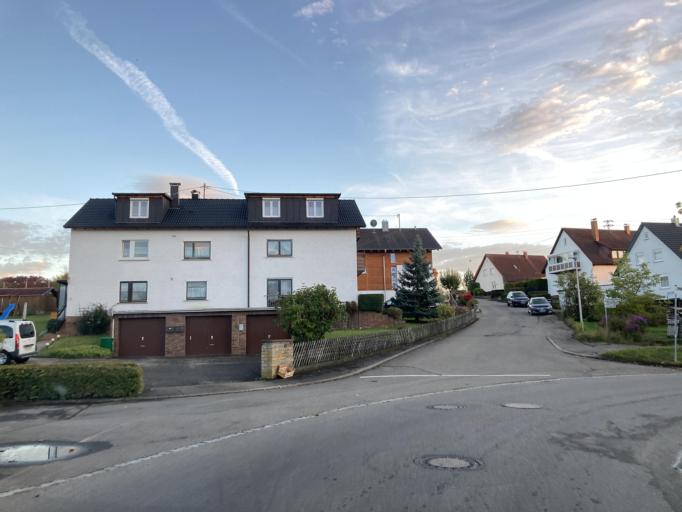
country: DE
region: Baden-Wuerttemberg
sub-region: Regierungsbezirk Stuttgart
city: Bondorf
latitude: 48.4950
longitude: 8.8131
